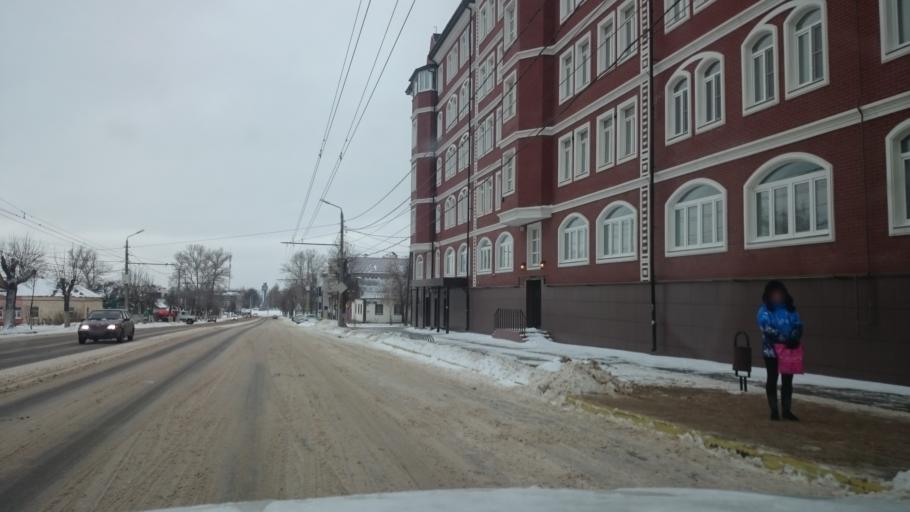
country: RU
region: Tula
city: Mendeleyevskiy
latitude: 54.1818
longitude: 37.5731
